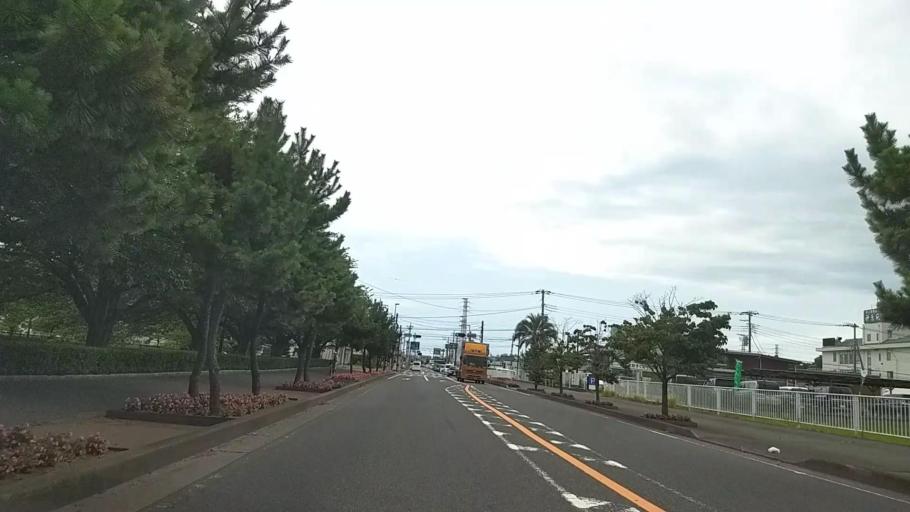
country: JP
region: Kanagawa
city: Chigasaki
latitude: 35.3744
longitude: 139.3837
